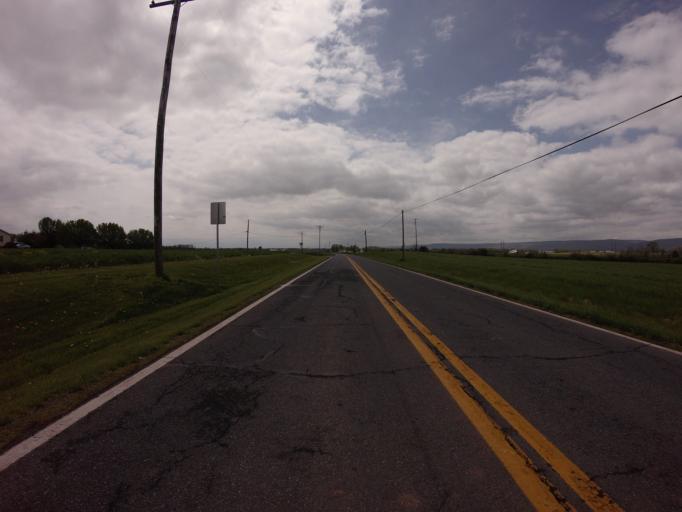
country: US
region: Maryland
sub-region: Frederick County
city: Thurmont
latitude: 39.5997
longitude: -77.3557
